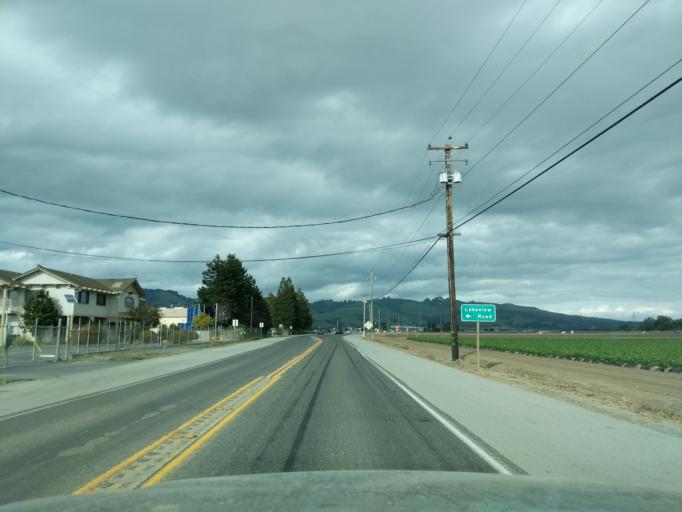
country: US
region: California
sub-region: Monterey County
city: Pajaro
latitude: 36.9166
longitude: -121.7337
